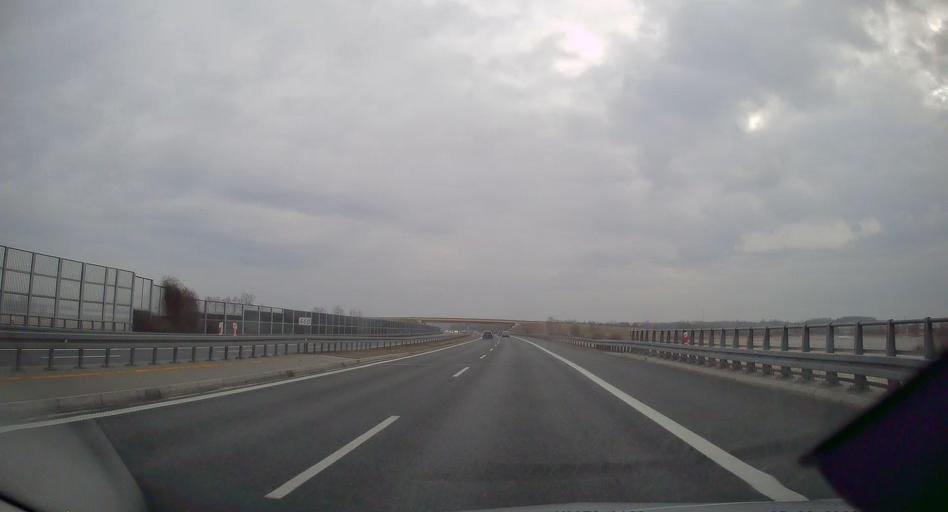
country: PL
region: Lesser Poland Voivodeship
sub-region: Powiat bochenski
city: Krzeczow
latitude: 50.0028
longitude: 20.4830
